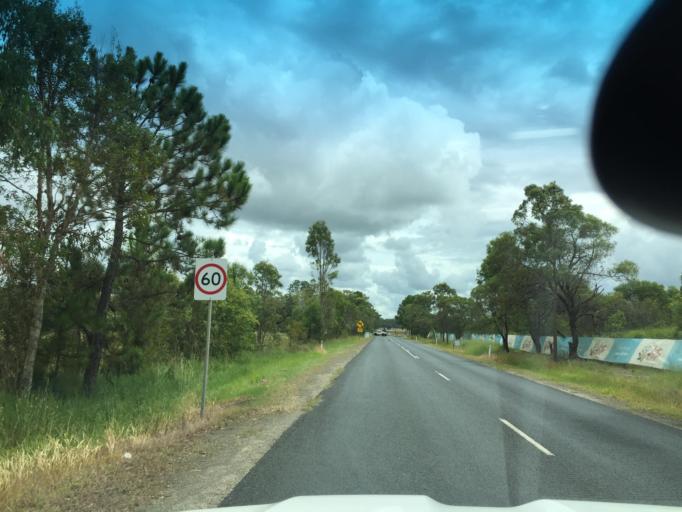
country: AU
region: Queensland
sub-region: Moreton Bay
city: Morayfield
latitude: -27.1119
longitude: 152.9802
